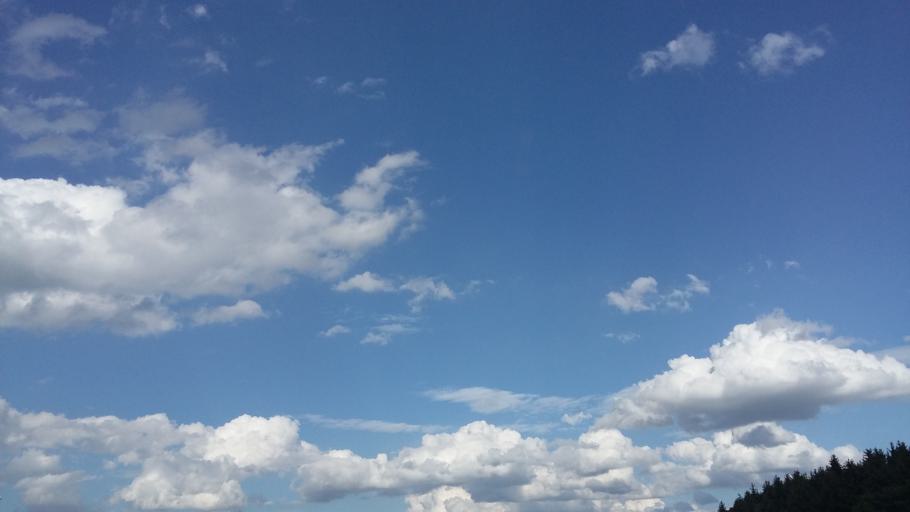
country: DE
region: Bavaria
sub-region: Swabia
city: Aystetten
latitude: 48.4200
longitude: 10.7965
